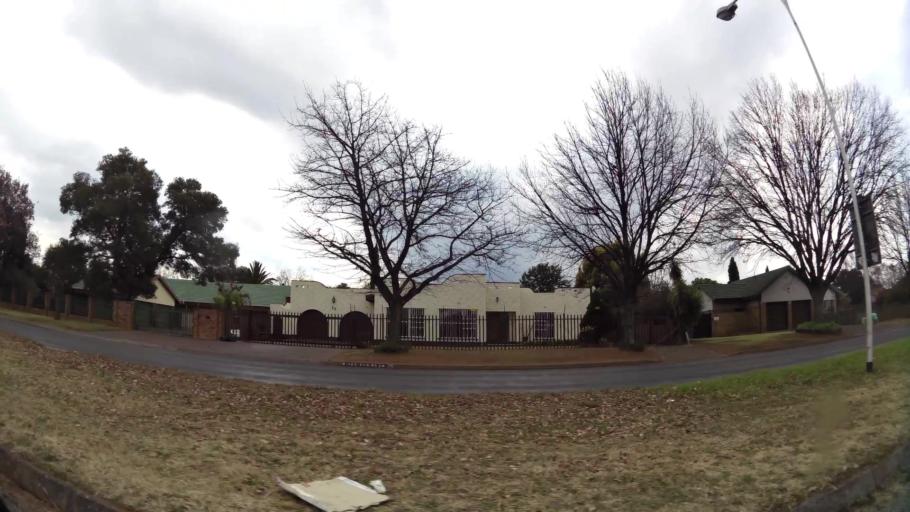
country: ZA
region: Gauteng
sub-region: Sedibeng District Municipality
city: Vanderbijlpark
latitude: -26.7318
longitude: 27.8480
